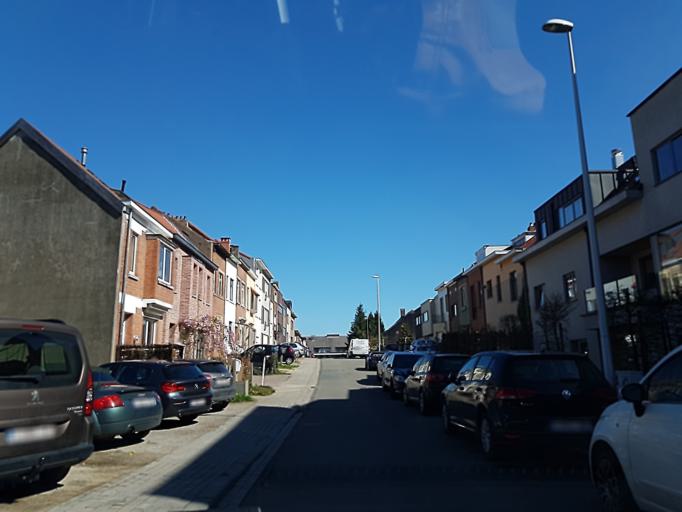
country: BE
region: Flanders
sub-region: Provincie Vlaams-Brabant
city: Dilbeek
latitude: 50.8520
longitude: 4.2618
